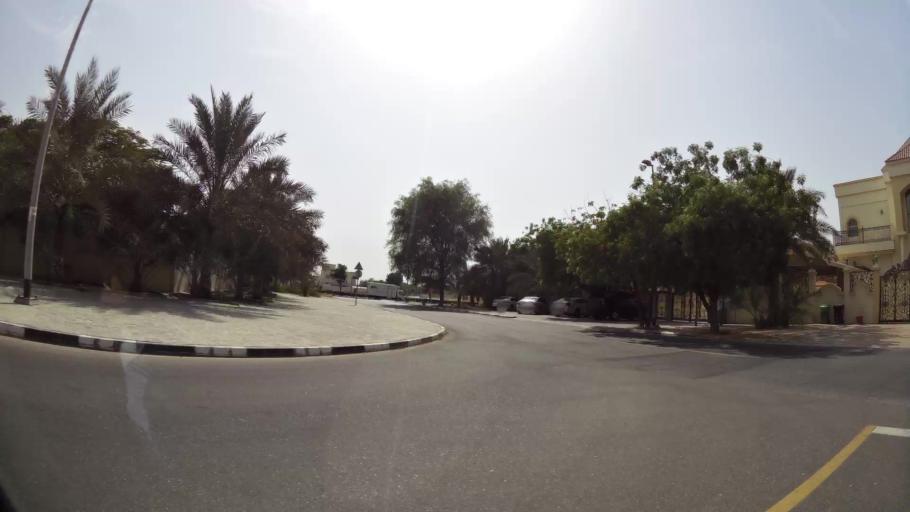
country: AE
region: Ash Shariqah
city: Sharjah
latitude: 25.2501
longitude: 55.4317
